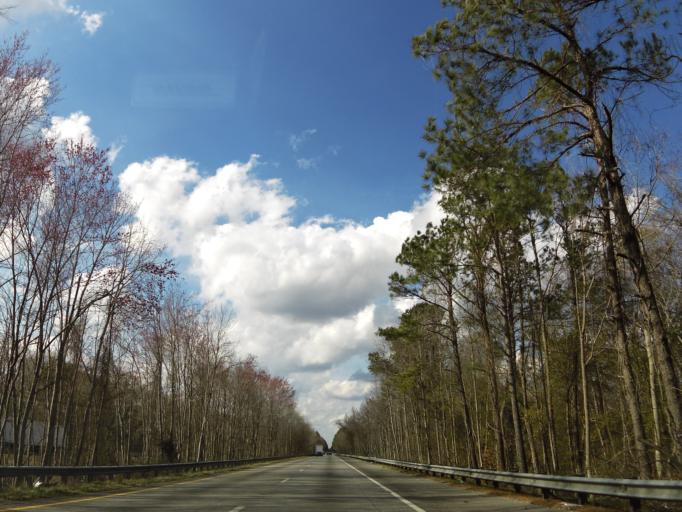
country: US
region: South Carolina
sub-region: Dorchester County
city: Ridgeville
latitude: 33.0978
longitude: -80.2377
